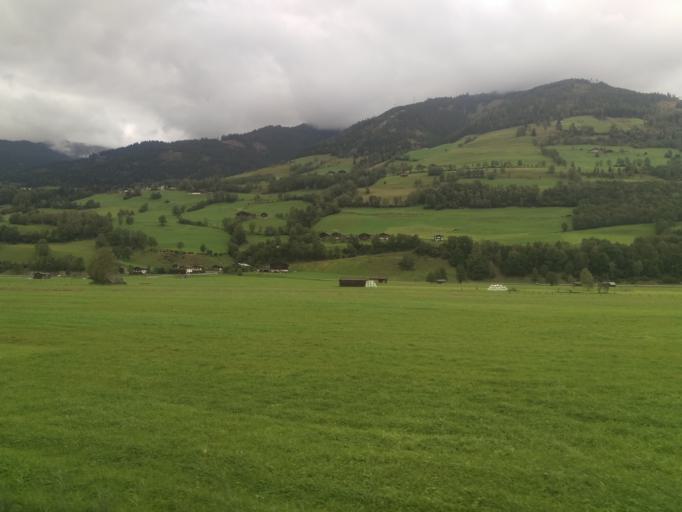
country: AT
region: Salzburg
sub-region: Politischer Bezirk Zell am See
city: Uttendorf
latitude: 47.2804
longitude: 12.6005
